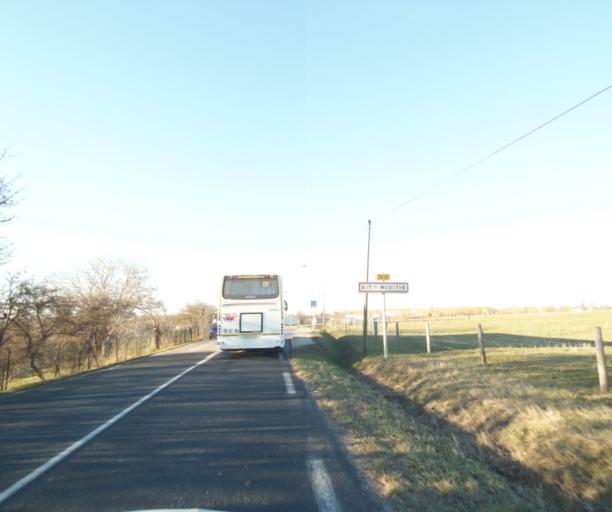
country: FR
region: Lorraine
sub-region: Departement de Meurthe-et-Moselle
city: Art-sur-Meurthe
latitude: 48.6513
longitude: 6.2707
